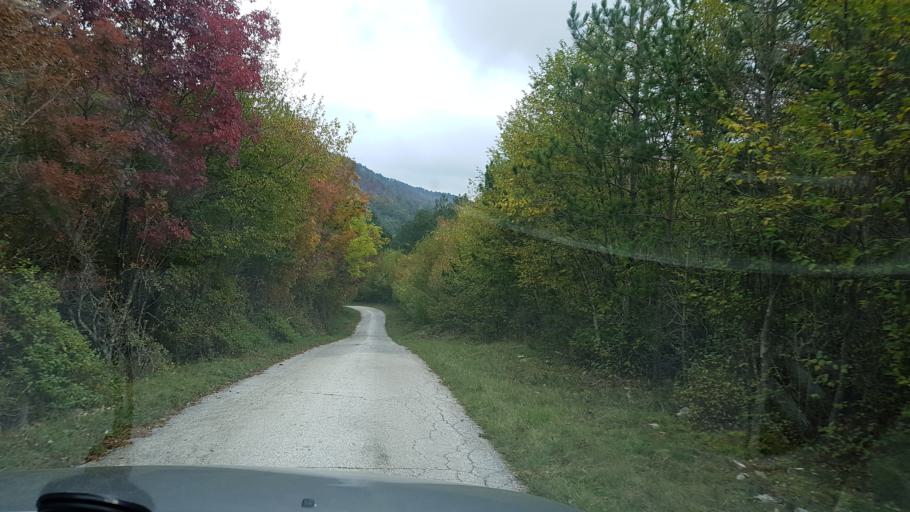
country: HR
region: Istarska
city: Buzet
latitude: 45.4472
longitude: 14.0324
